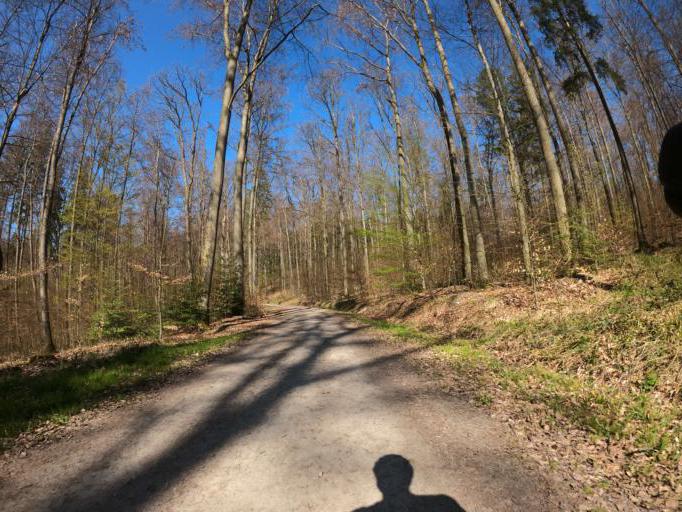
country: DE
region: Baden-Wuerttemberg
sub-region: Karlsruhe Region
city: Wiernsheim
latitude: 48.8924
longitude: 8.8274
